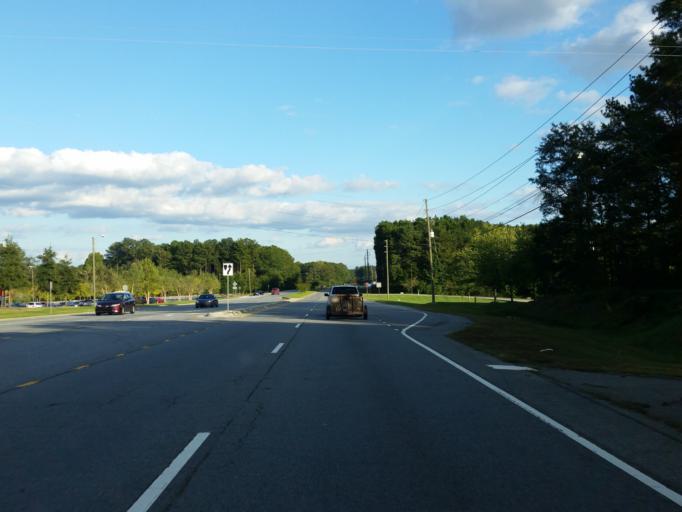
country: US
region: Georgia
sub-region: Cobb County
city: Powder Springs
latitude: 33.9012
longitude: -84.6629
